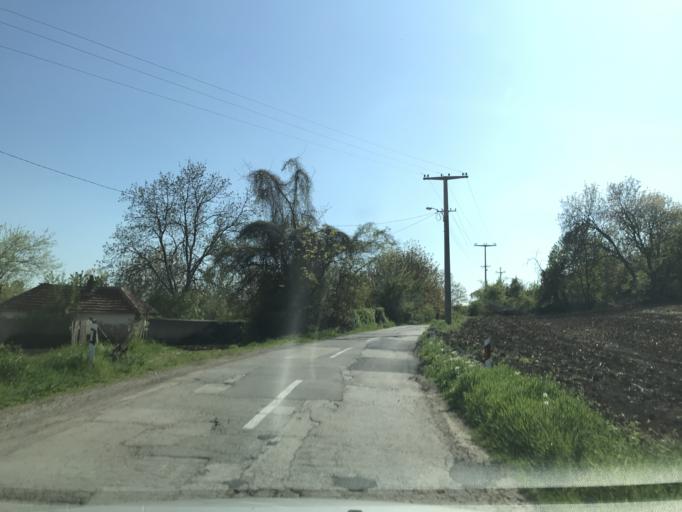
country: RS
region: Central Serbia
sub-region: Nisavski Okrug
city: Nis
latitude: 43.4080
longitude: 21.8100
